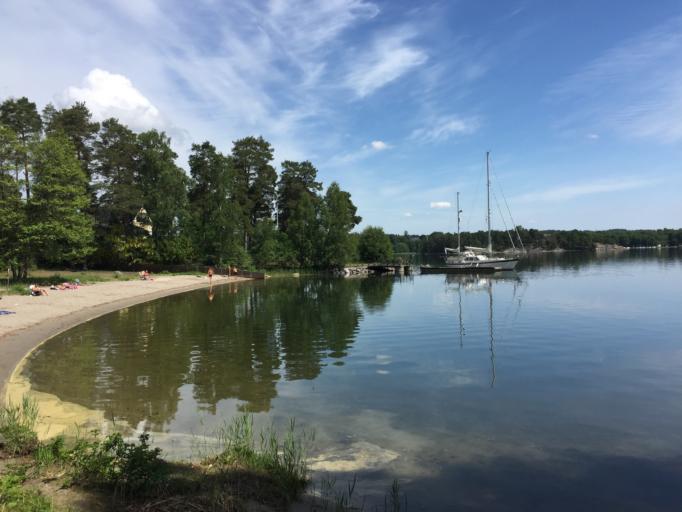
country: SE
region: Stockholm
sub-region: Sodertalje Kommun
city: Pershagen
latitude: 59.1581
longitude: 17.6603
